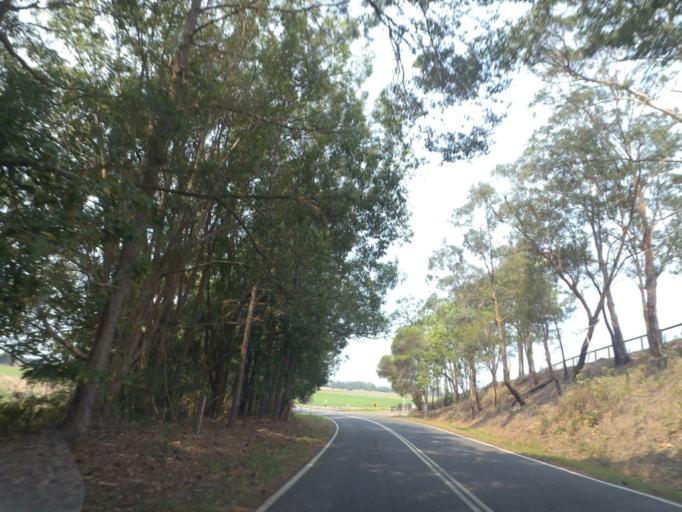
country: AU
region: New South Wales
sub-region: Tweed
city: Burringbar
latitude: -28.4578
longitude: 153.5260
